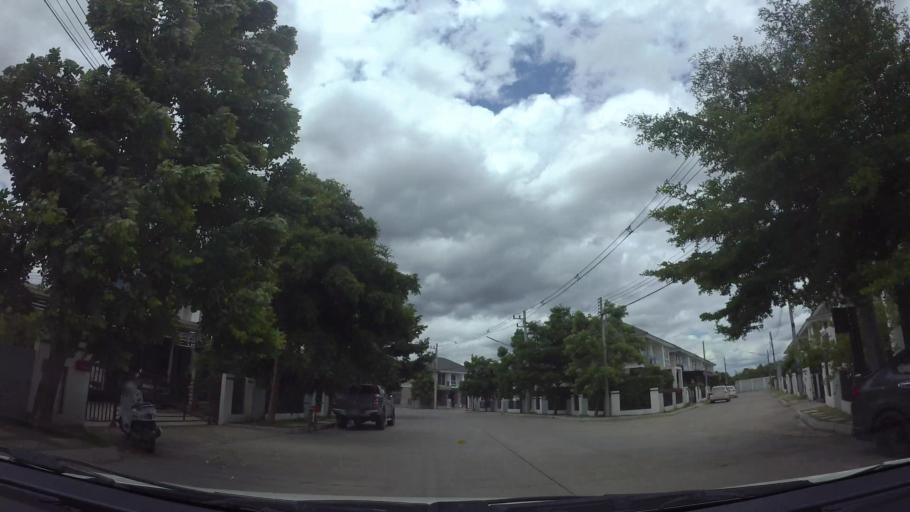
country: TH
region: Chiang Mai
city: Saraphi
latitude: 18.7478
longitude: 99.0426
